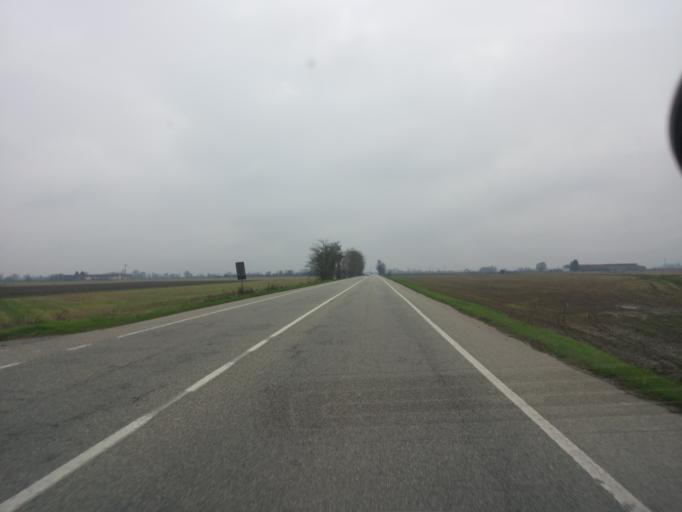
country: IT
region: Piedmont
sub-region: Provincia di Vercelli
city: Stroppiana
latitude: 45.2170
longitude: 8.4560
